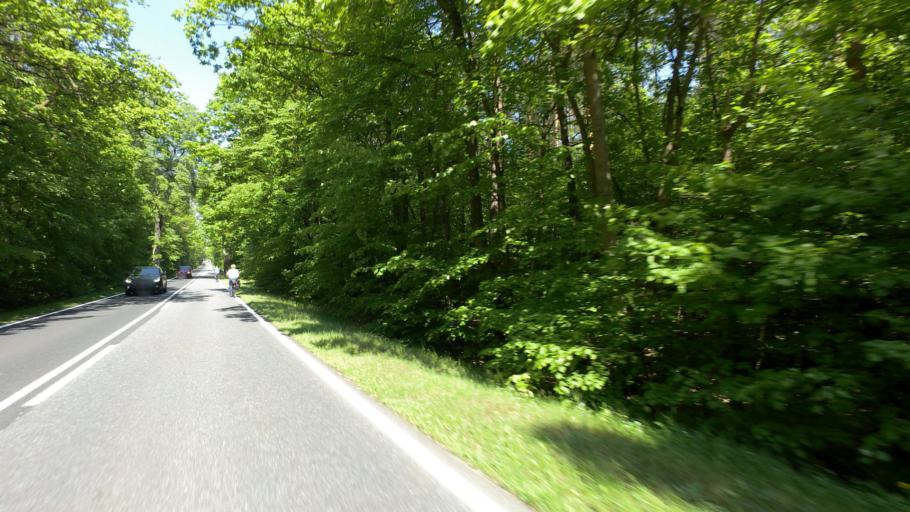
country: DE
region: Brandenburg
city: Furstenberg
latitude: 53.1384
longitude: 13.1571
